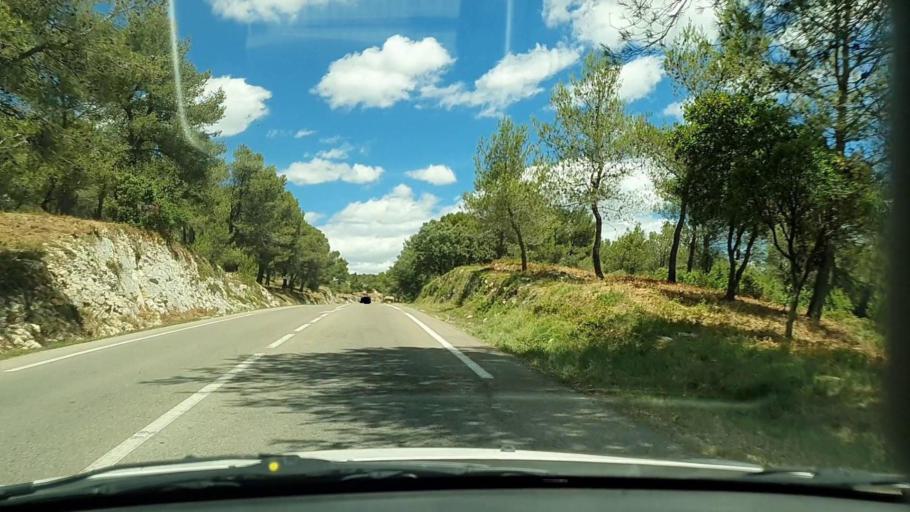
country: FR
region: Languedoc-Roussillon
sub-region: Departement du Gard
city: Poulx
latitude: 43.8935
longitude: 4.4199
